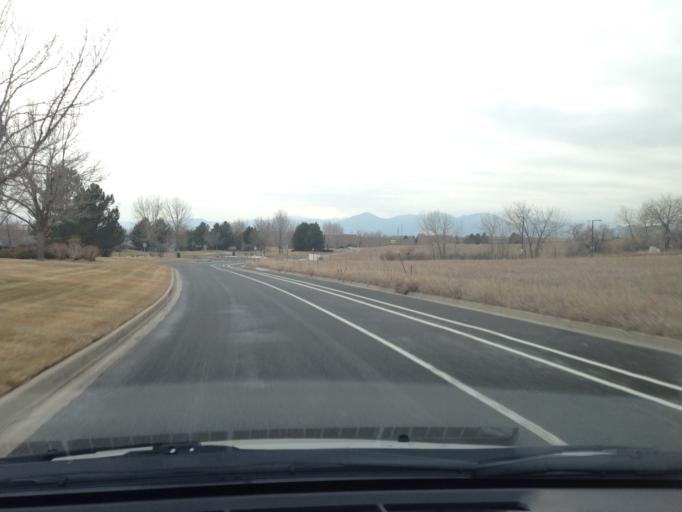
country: US
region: Colorado
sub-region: Boulder County
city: Superior
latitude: 39.9701
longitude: -105.1681
